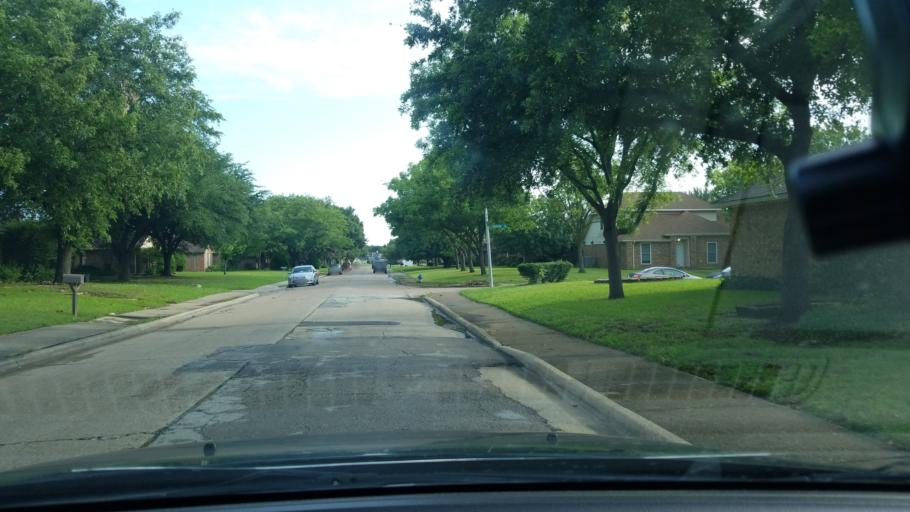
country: US
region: Texas
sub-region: Dallas County
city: Mesquite
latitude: 32.7995
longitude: -96.6088
